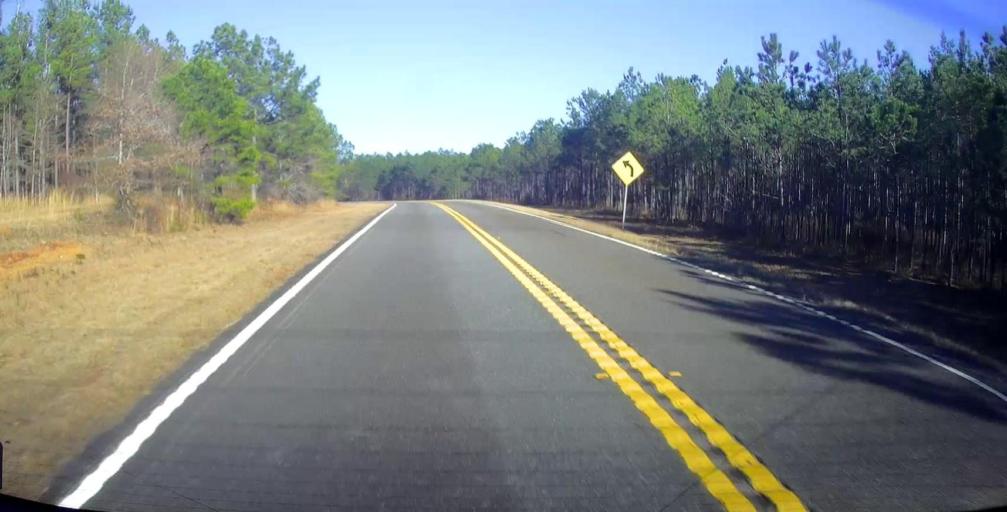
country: US
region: Georgia
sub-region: Talbot County
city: Talbotton
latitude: 32.6462
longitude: -84.4158
